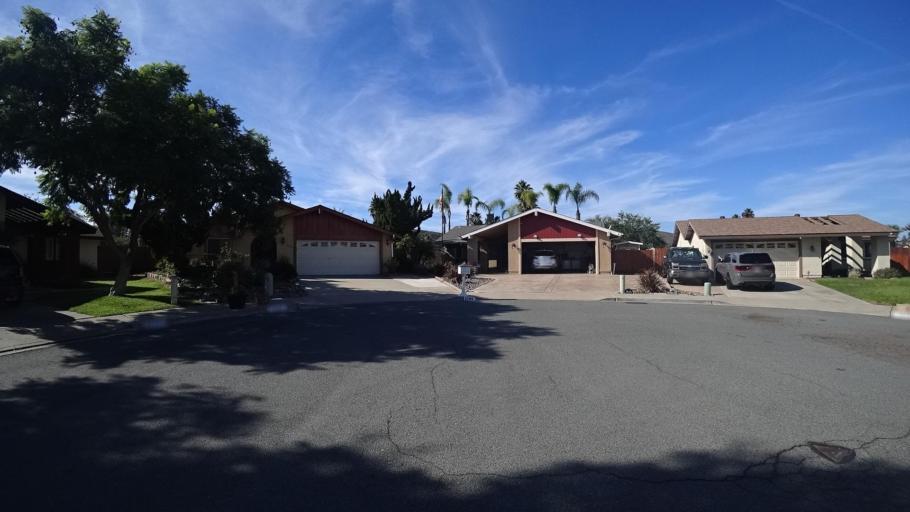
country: US
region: California
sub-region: San Diego County
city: Spring Valley
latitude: 32.7285
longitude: -116.9800
